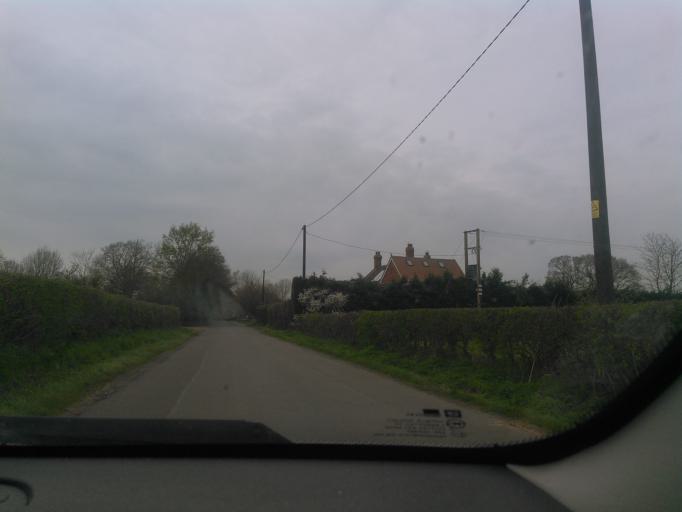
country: GB
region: England
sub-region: Shropshire
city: Shawbury
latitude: 52.7988
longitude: -2.5863
